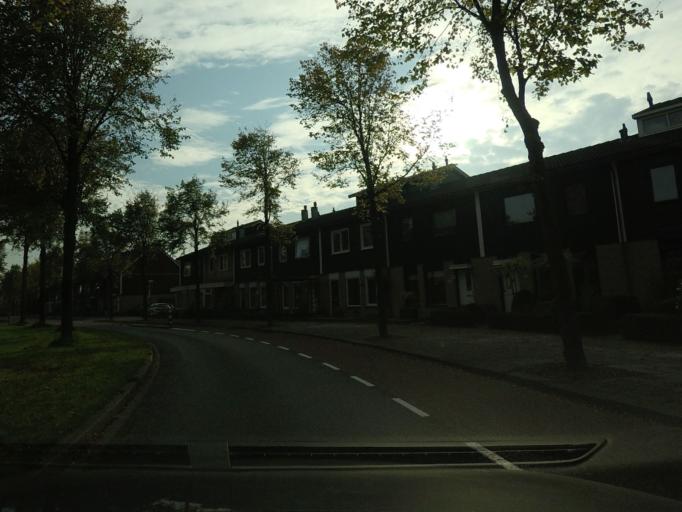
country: NL
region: North Holland
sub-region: Gemeente Alkmaar
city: Alkmaar
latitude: 52.6711
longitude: 4.7622
